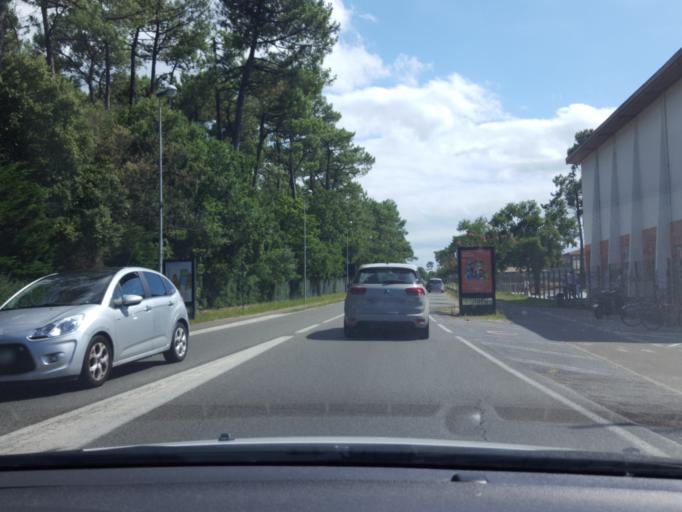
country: FR
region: Aquitaine
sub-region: Departement des Landes
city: Capbreton
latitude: 43.6514
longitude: -1.4272
